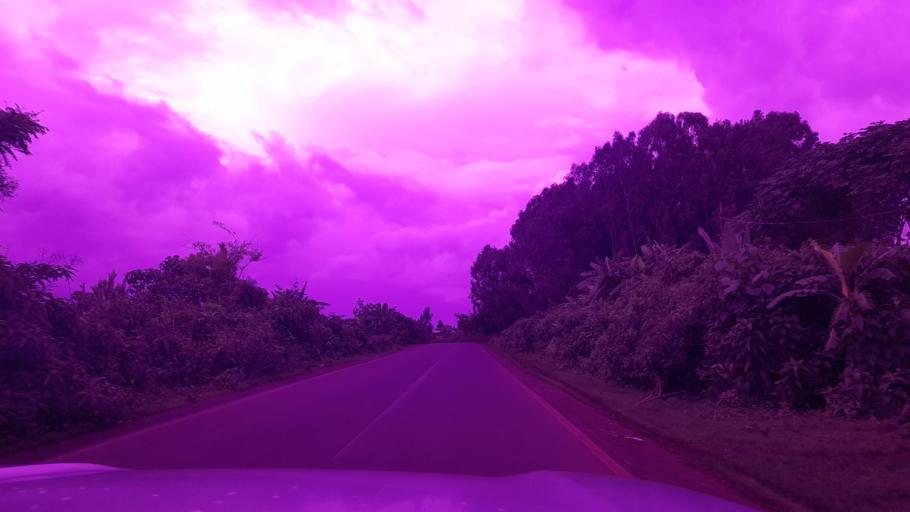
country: ET
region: Oromiya
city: Jima
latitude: 7.9077
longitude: 37.3939
